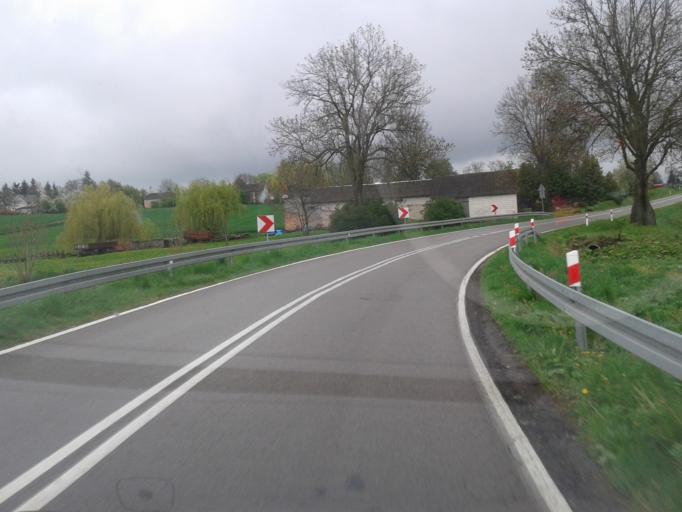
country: PL
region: Lublin Voivodeship
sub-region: Powiat hrubieszowski
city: Dolhobyczow
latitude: 50.5862
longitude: 23.9712
